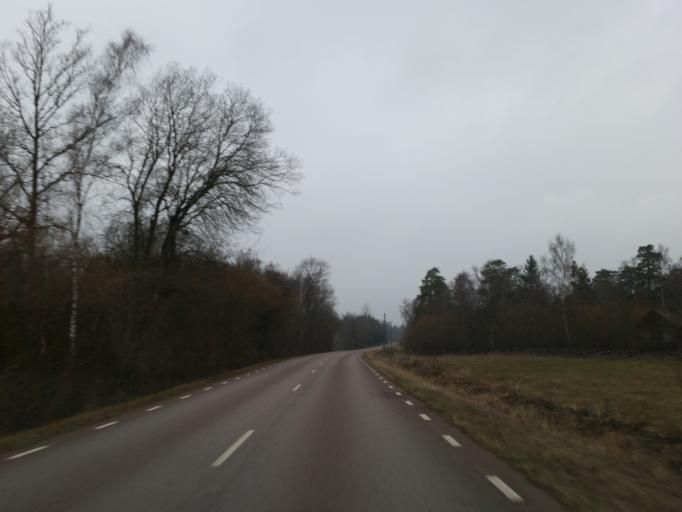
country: SE
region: Kalmar
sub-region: Morbylanga Kommun
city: Sodra Sandby
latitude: 56.6232
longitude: 16.6026
